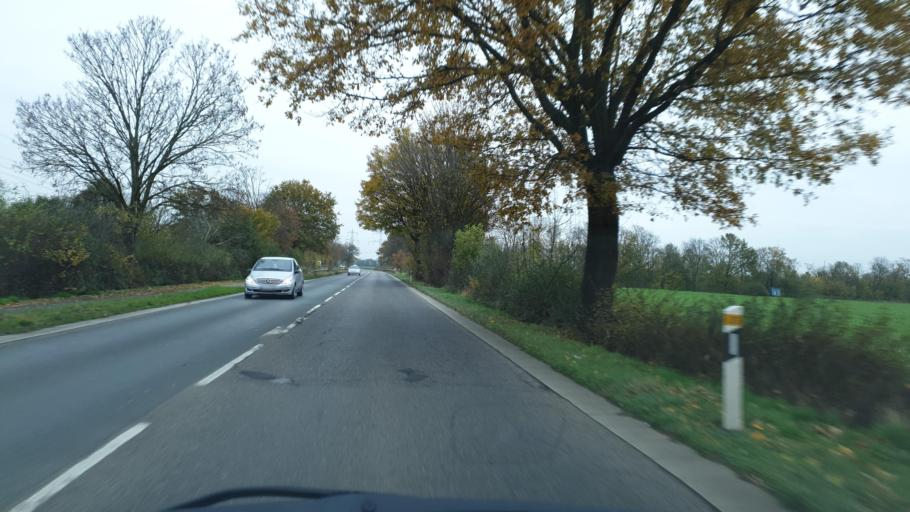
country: DE
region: North Rhine-Westphalia
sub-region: Regierungsbezirk Koln
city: Frechen
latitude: 50.8998
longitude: 6.8433
